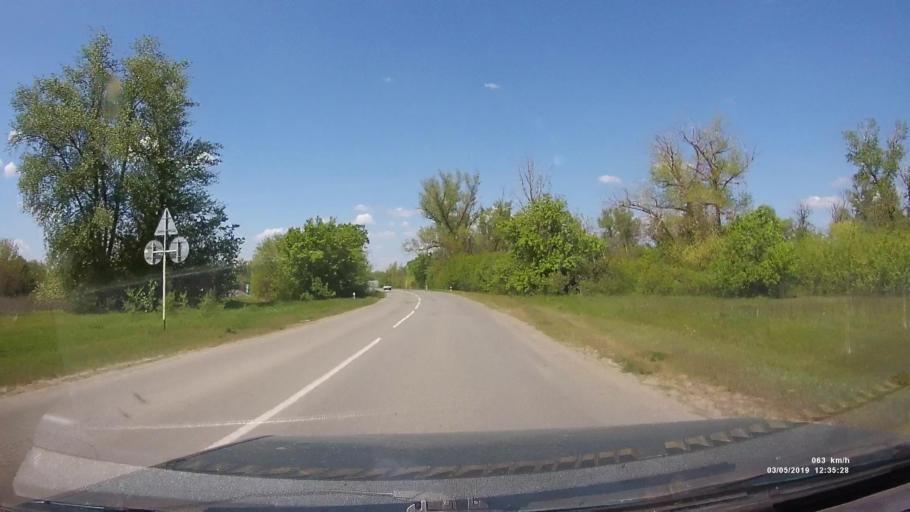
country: RU
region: Rostov
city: Semikarakorsk
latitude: 47.5270
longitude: 40.7607
